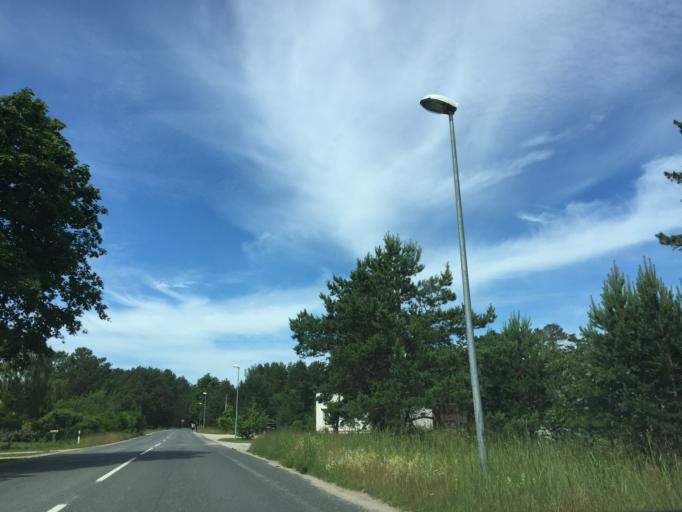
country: LV
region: Dundaga
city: Dundaga
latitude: 57.6523
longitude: 22.5734
